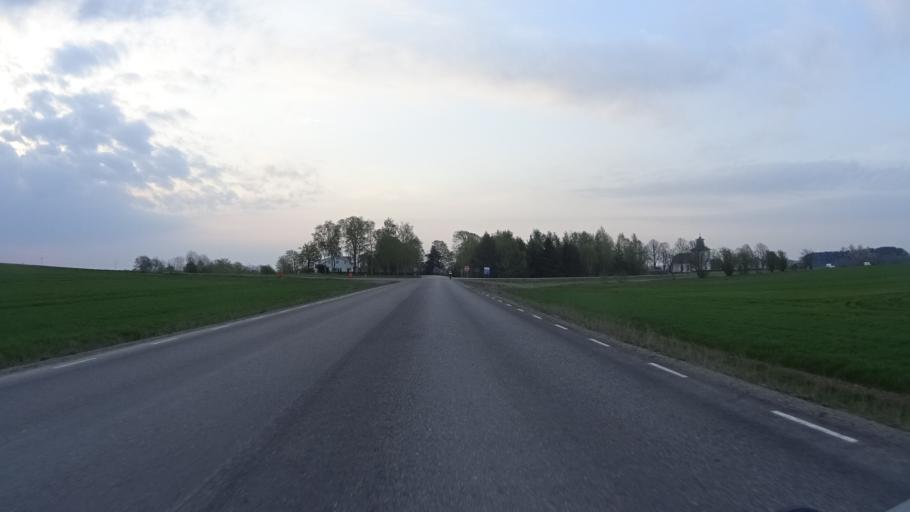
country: SE
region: Vaestra Goetaland
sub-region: Gotene Kommun
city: Kallby
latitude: 58.4967
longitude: 13.3119
